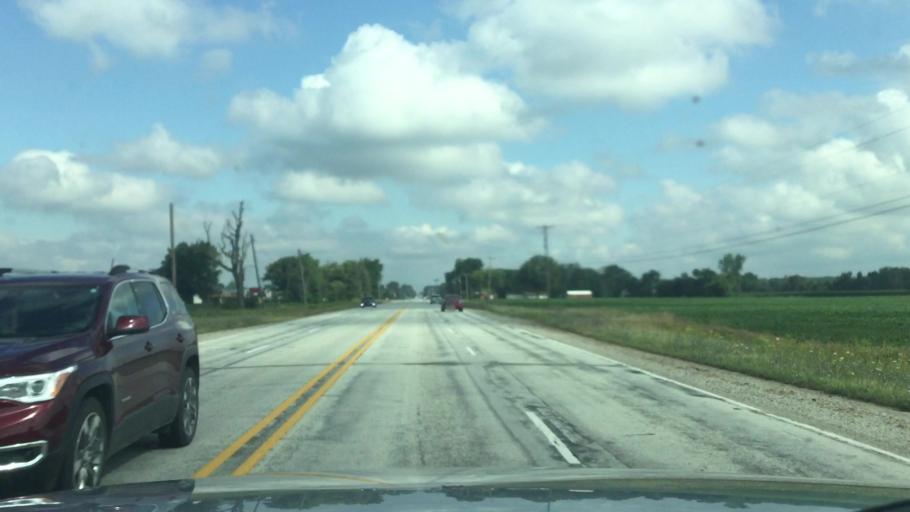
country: US
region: Michigan
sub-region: Saginaw County
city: Birch Run
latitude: 43.2406
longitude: -83.7620
